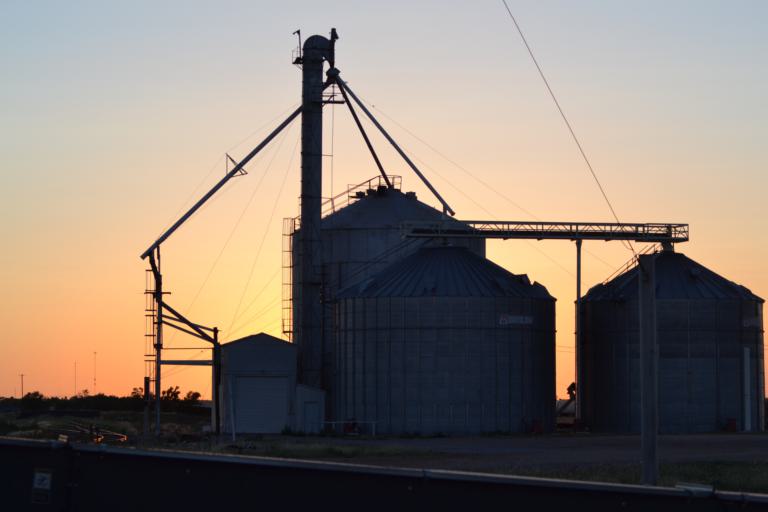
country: US
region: Texas
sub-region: Hardeman County
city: Quanah
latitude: 34.3325
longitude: -99.8862
